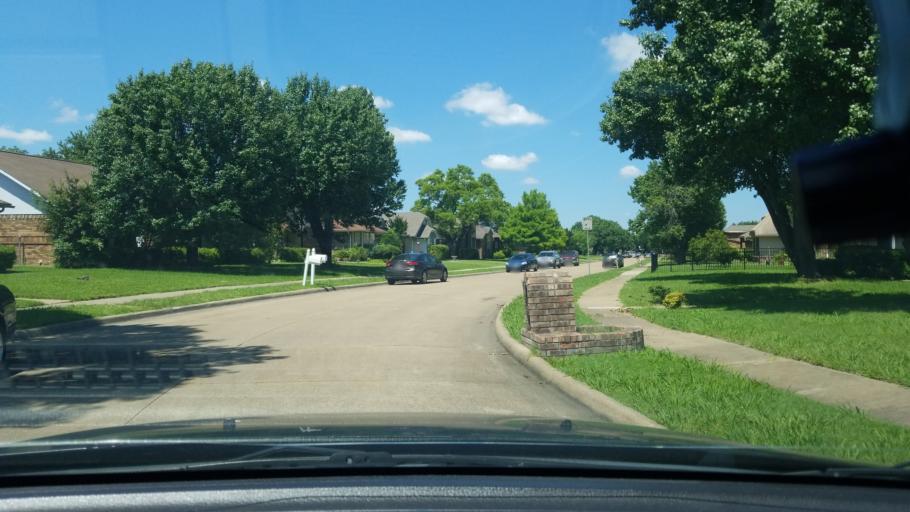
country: US
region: Texas
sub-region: Dallas County
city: Mesquite
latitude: 32.7962
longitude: -96.5984
